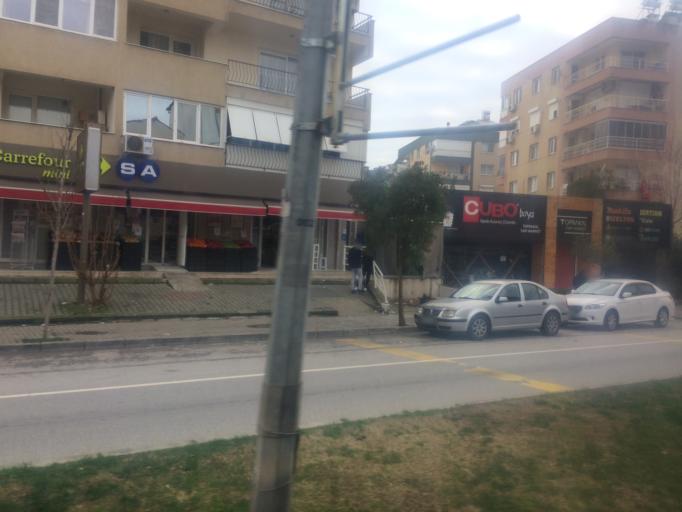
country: TR
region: Izmir
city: Karsiyaka
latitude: 38.4931
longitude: 27.0571
